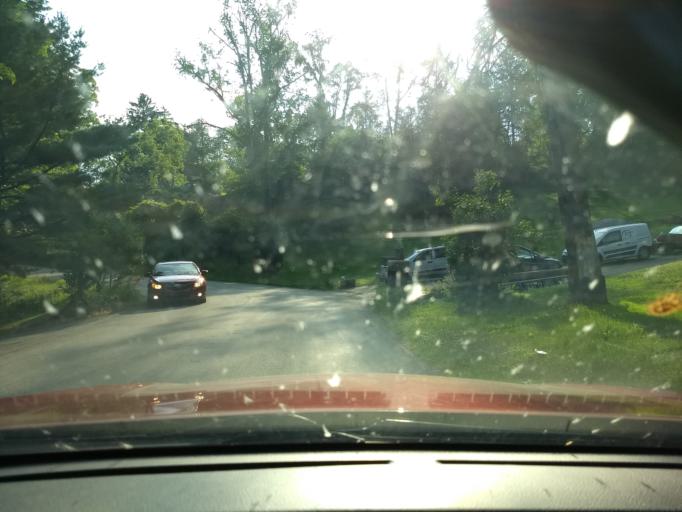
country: US
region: Pennsylvania
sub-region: Westmoreland County
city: Trafford
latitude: 40.3640
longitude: -79.7667
